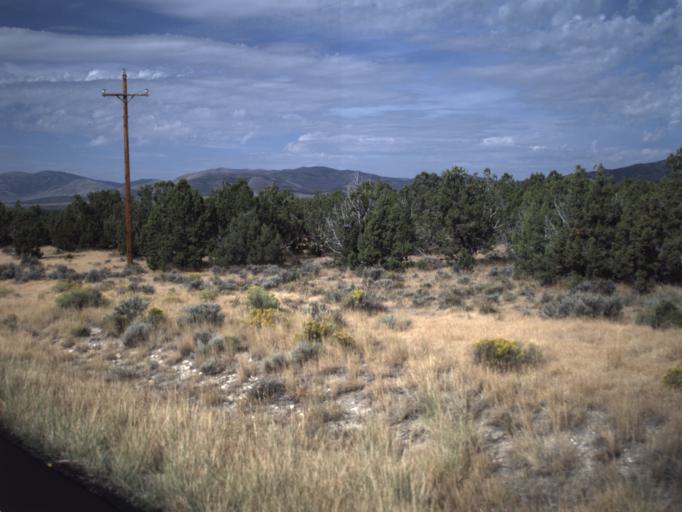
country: US
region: Idaho
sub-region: Cassia County
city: Burley
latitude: 41.8114
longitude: -113.4417
